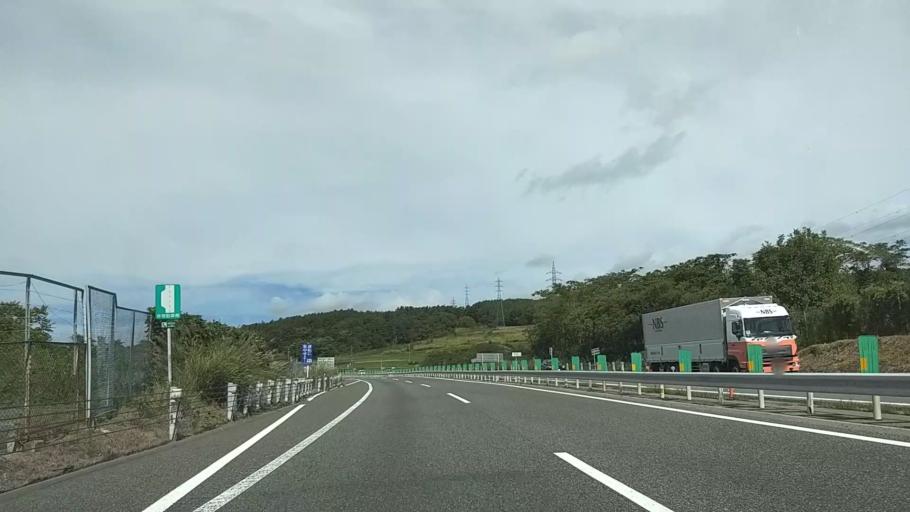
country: JP
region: Nagano
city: Chino
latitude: 35.8857
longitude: 138.2986
